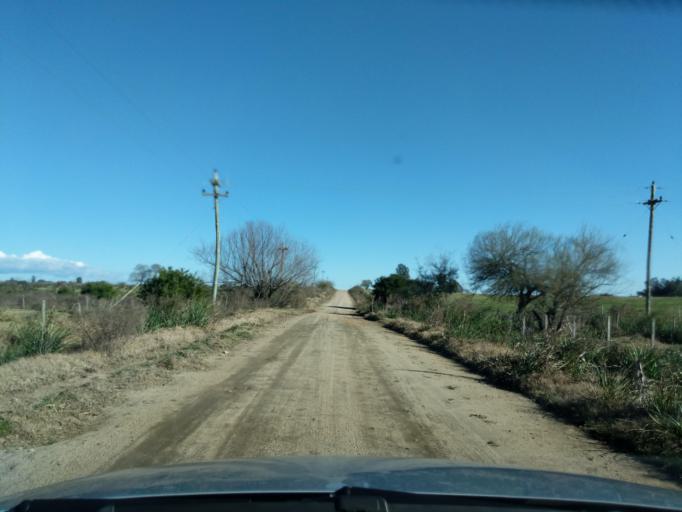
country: UY
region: Florida
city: Florida
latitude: -34.0802
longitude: -56.2602
